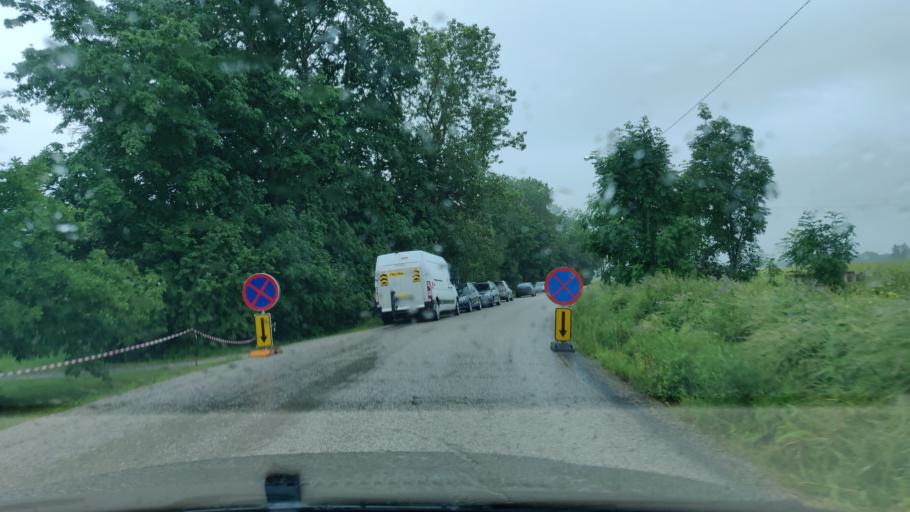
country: EE
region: Jaervamaa
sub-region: Jaerva-Jaani vald
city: Jarva-Jaani
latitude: 59.0952
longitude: 25.6989
